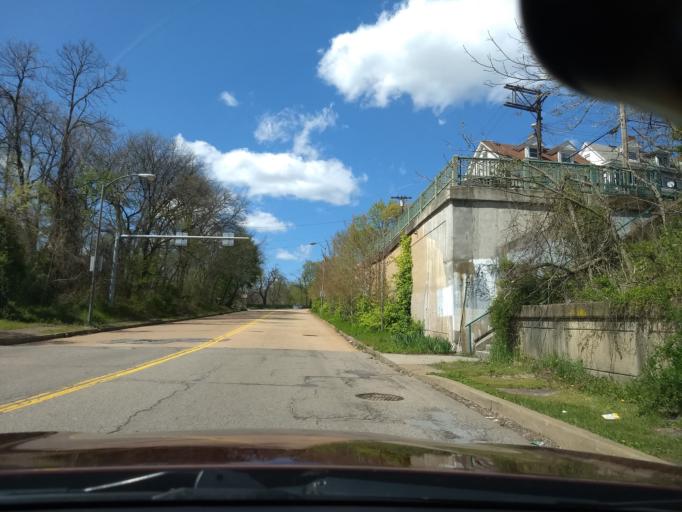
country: US
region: Pennsylvania
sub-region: Allegheny County
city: Bellevue
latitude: 40.4794
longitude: -80.0429
